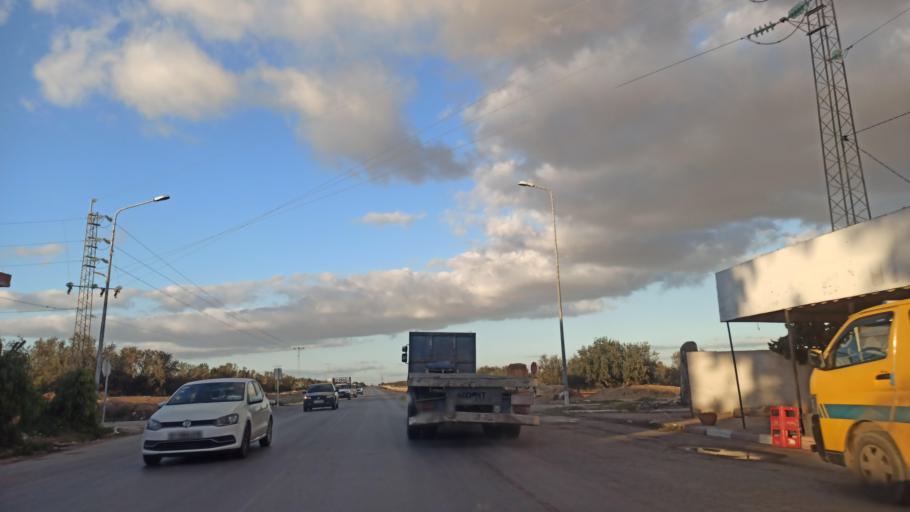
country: TN
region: Susah
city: Sidi Bou Ali
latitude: 35.9356
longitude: 10.3010
